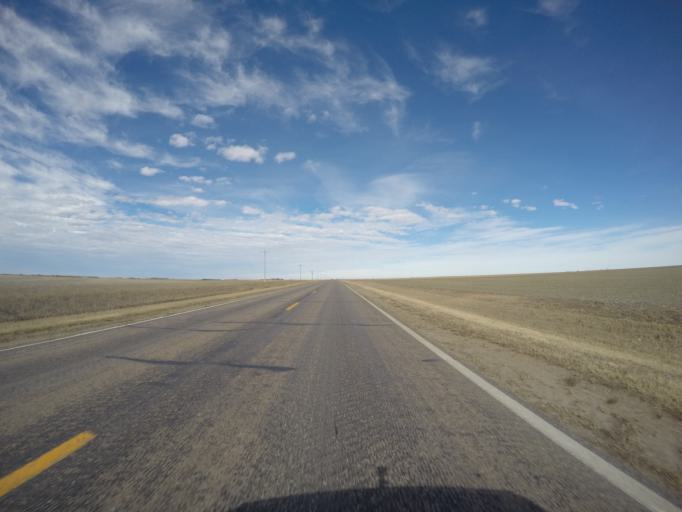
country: US
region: Nebraska
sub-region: Franklin County
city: Franklin
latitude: 40.2253
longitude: -98.9524
